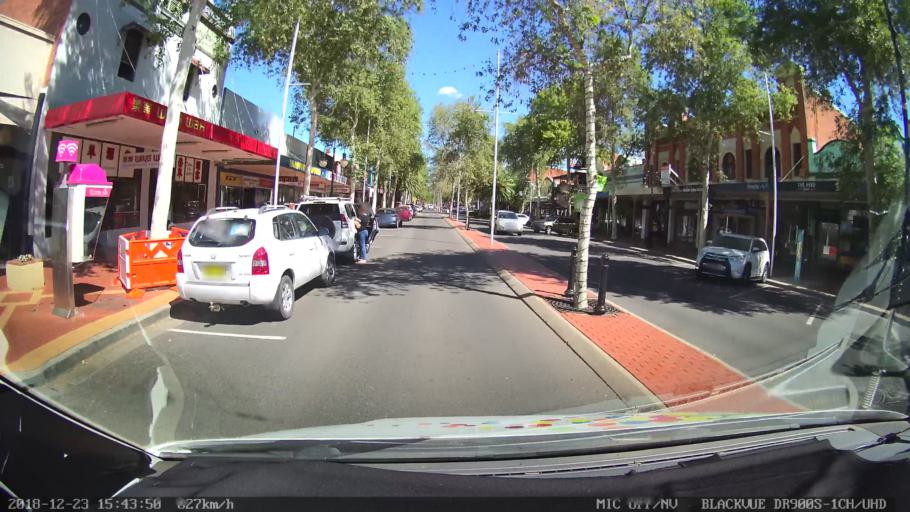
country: AU
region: New South Wales
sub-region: Tamworth Municipality
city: Tamworth
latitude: -31.0886
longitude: 150.9282
